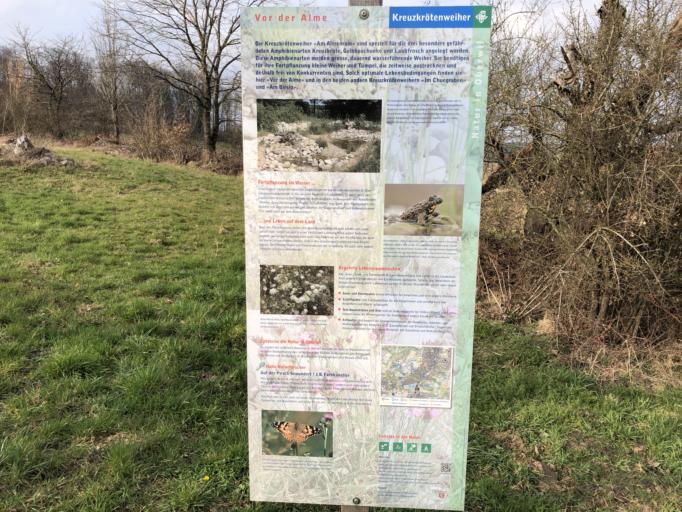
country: CH
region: Basel-Landschaft
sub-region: Bezirk Arlesheim
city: Oberwil
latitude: 47.5172
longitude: 7.5420
